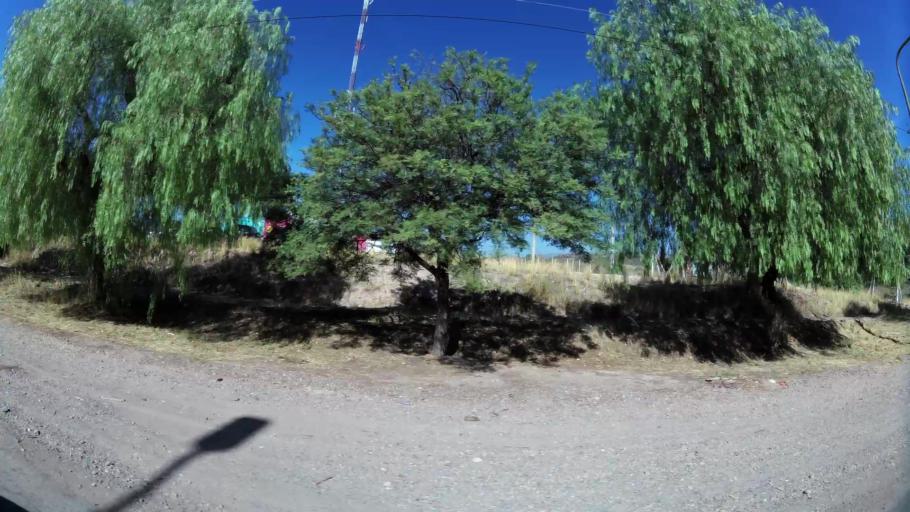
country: AR
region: Mendoza
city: Mendoza
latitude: -32.8947
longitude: -68.8828
